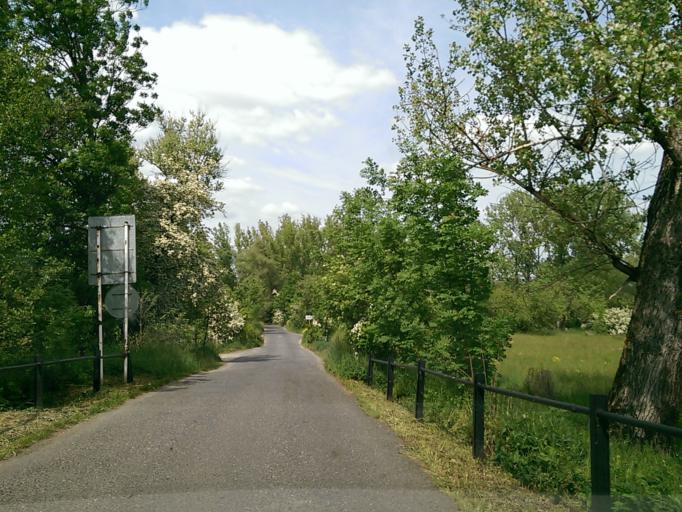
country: CZ
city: Prisovice
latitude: 50.5639
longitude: 15.0848
